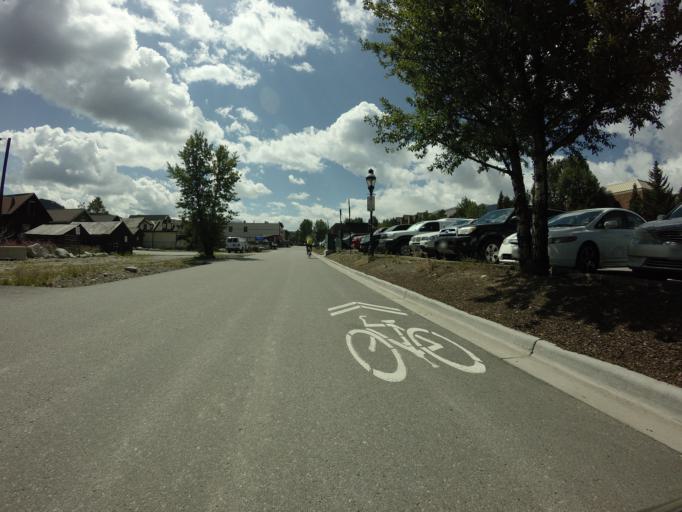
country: US
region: Colorado
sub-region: Summit County
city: Breckenridge
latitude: 39.4832
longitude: -106.0468
